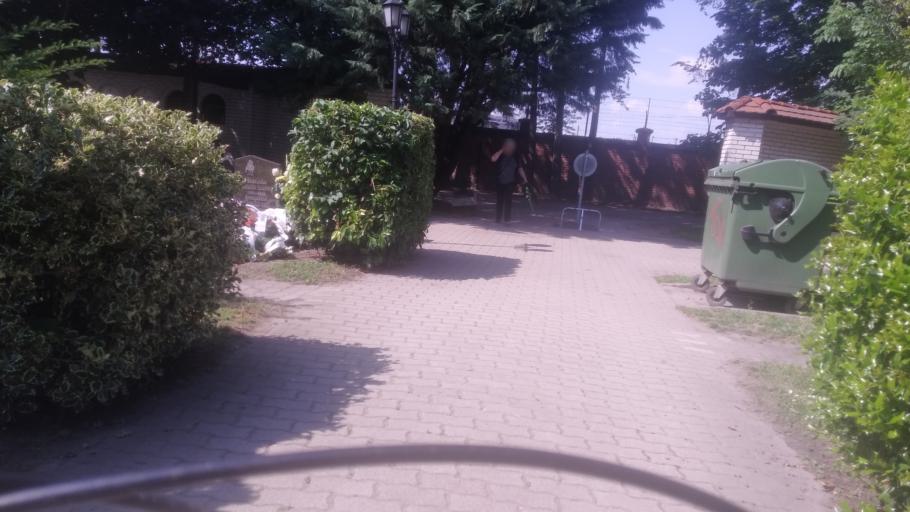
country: HU
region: Budapest
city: Budapest XIV. keruelet
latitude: 47.4944
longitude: 19.0985
